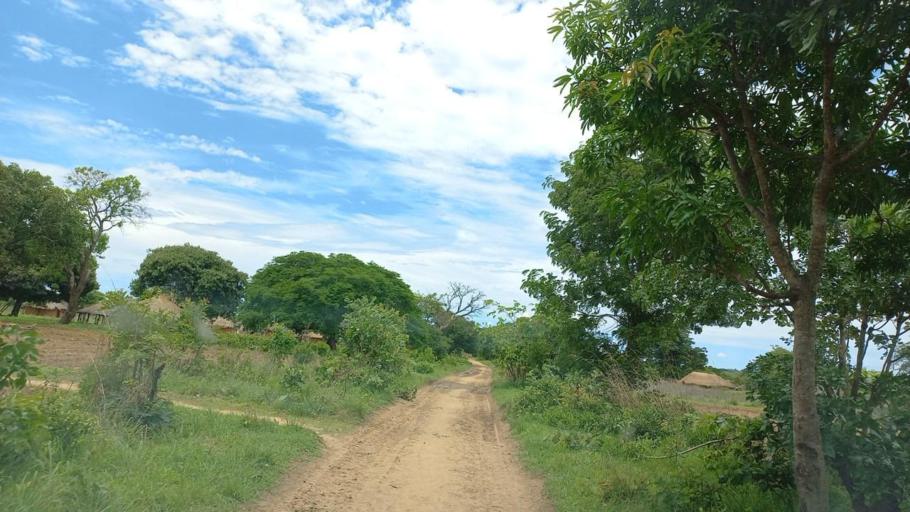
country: ZM
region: North-Western
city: Kabompo
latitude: -13.6226
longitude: 24.1887
